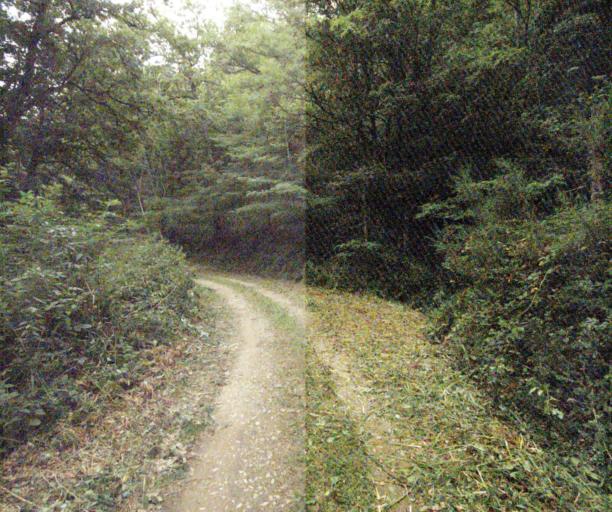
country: FR
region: Midi-Pyrenees
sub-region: Departement du Tarn
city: Soreze
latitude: 43.4178
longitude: 2.0648
